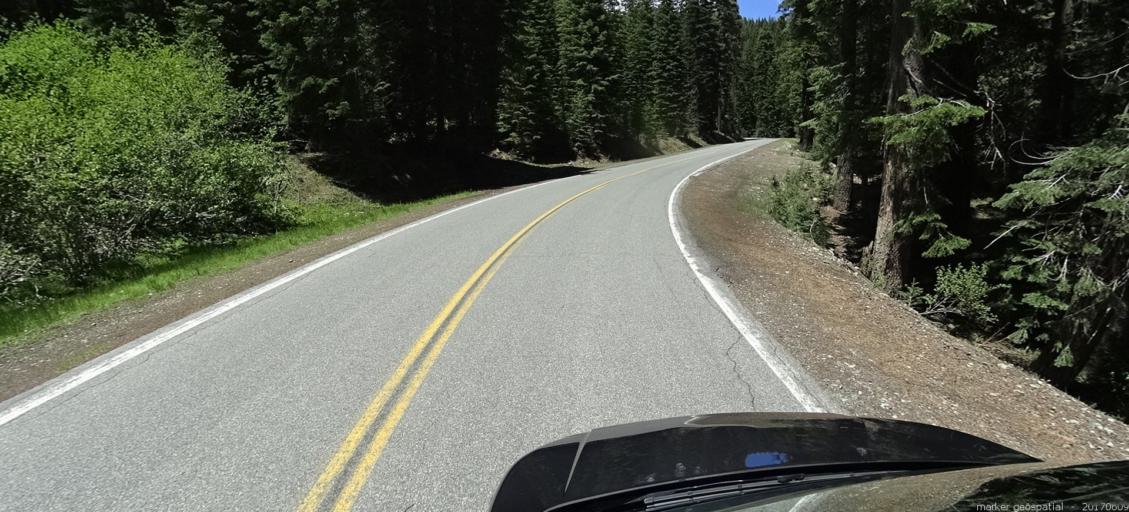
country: US
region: California
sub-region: Siskiyou County
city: Yreka
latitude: 41.4005
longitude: -122.9922
